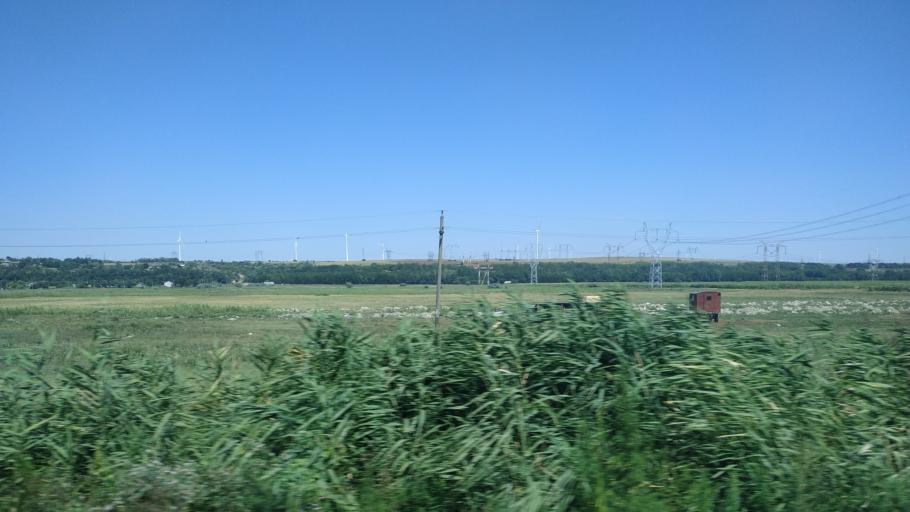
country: RO
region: Constanta
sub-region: Comuna Saligny
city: Faclia
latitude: 44.2703
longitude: 28.1179
